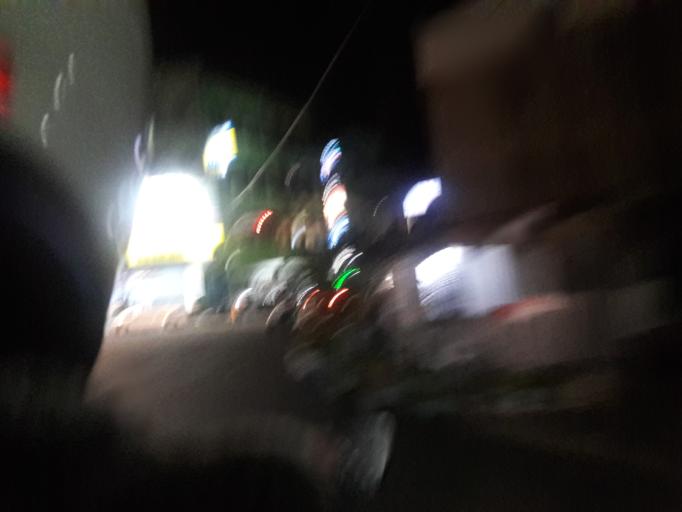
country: TW
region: Taiwan
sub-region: Miaoli
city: Miaoli
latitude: 24.4878
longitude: 120.6800
